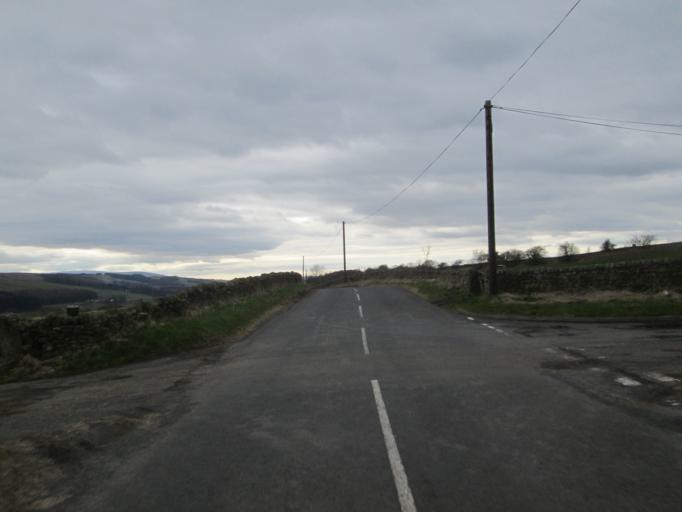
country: GB
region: England
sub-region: Northumberland
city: Bardon Mill
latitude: 54.9716
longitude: -2.3850
